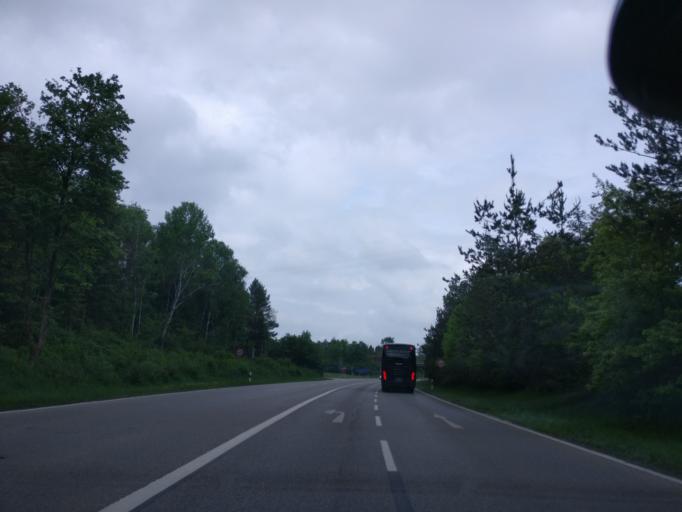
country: DE
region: Bavaria
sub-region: Upper Bavaria
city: Germering
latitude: 48.1149
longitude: 11.3849
